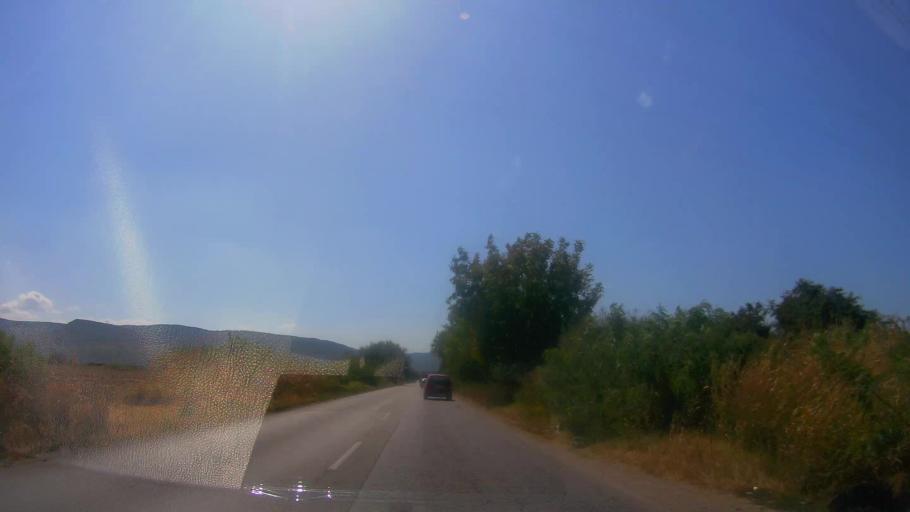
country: BG
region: Veliko Turnovo
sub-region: Obshtina Gorna Oryakhovitsa
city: Purvomaytsi
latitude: 43.1584
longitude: 25.6191
